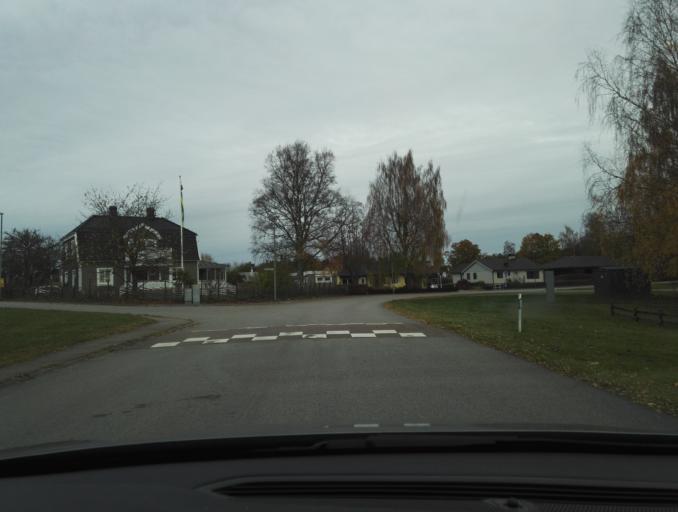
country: SE
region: Kronoberg
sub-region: Vaxjo Kommun
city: Vaexjoe
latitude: 56.9103
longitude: 14.7431
